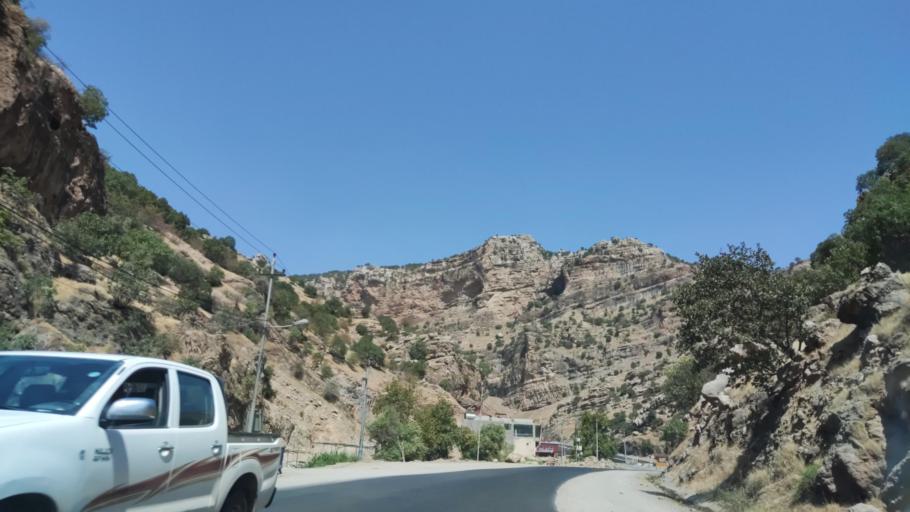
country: IQ
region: Arbil
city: Ruwandiz
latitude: 36.6285
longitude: 44.4496
